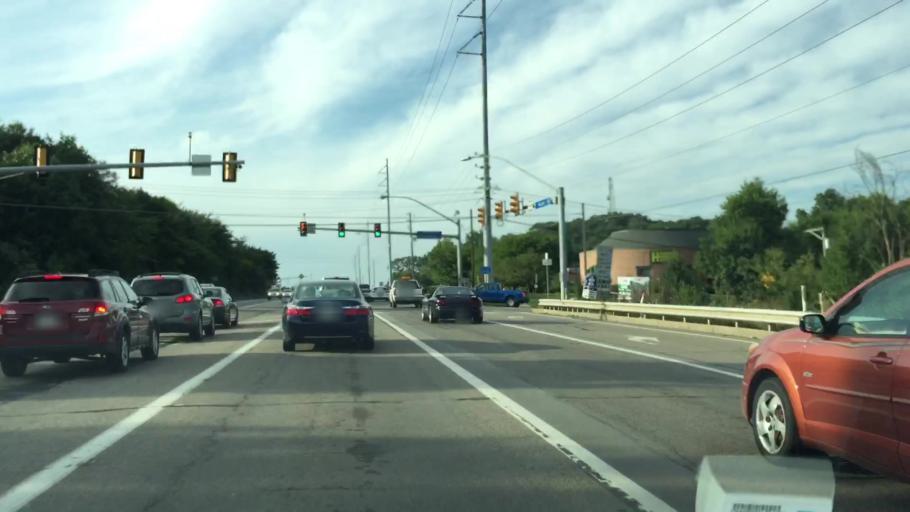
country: US
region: Pennsylvania
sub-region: Butler County
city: Fox Run
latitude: 40.7221
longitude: -80.1060
